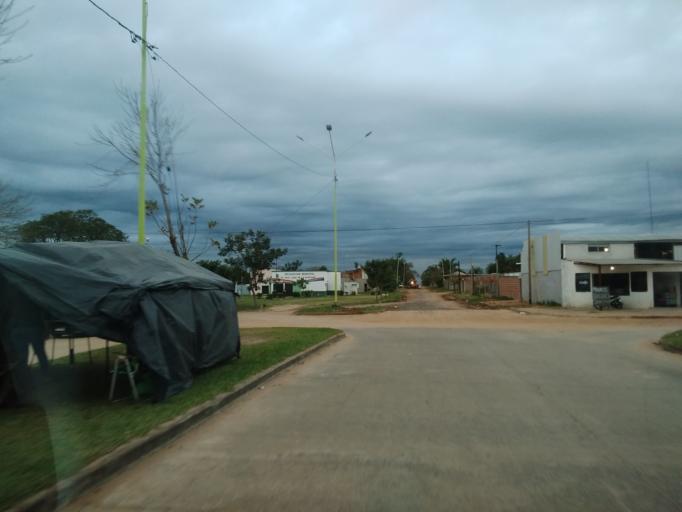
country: AR
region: Corrientes
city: Corrientes
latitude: -27.5090
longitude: -58.7928
